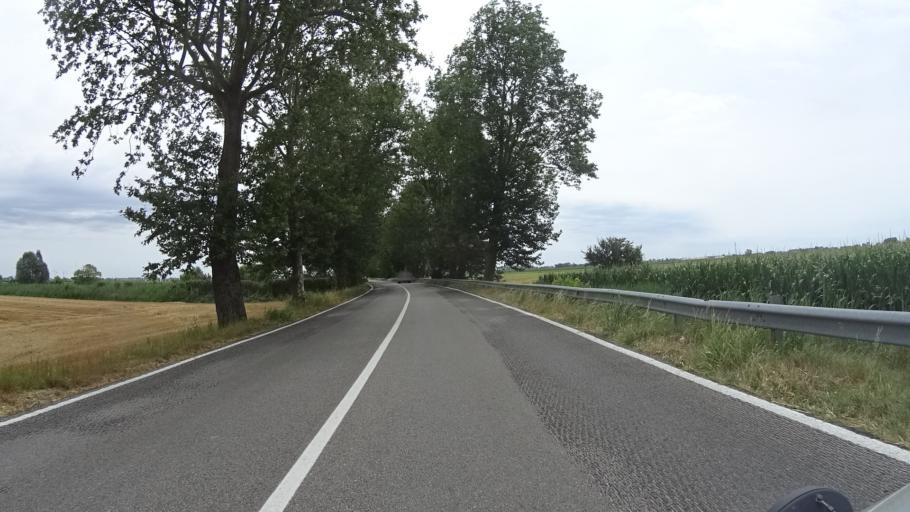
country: IT
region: Veneto
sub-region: Provincia di Venezia
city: San Giorgio di Livenza
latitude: 45.6798
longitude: 12.7845
